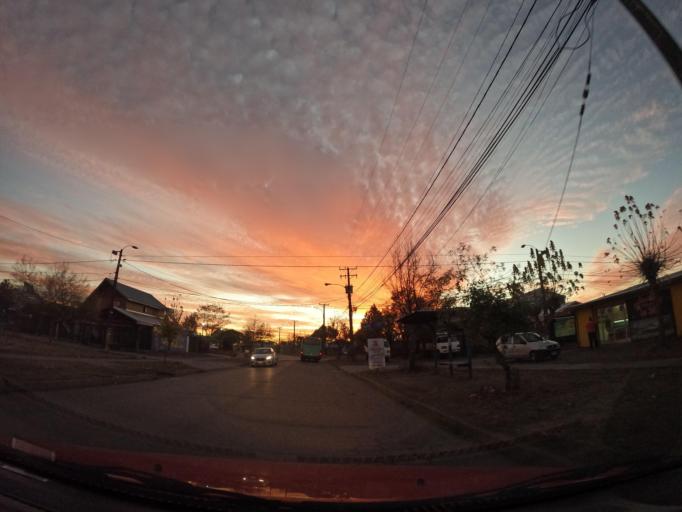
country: CL
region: Biobio
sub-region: Provincia de Nuble
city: Chillan
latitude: -36.6299
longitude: -72.1022
